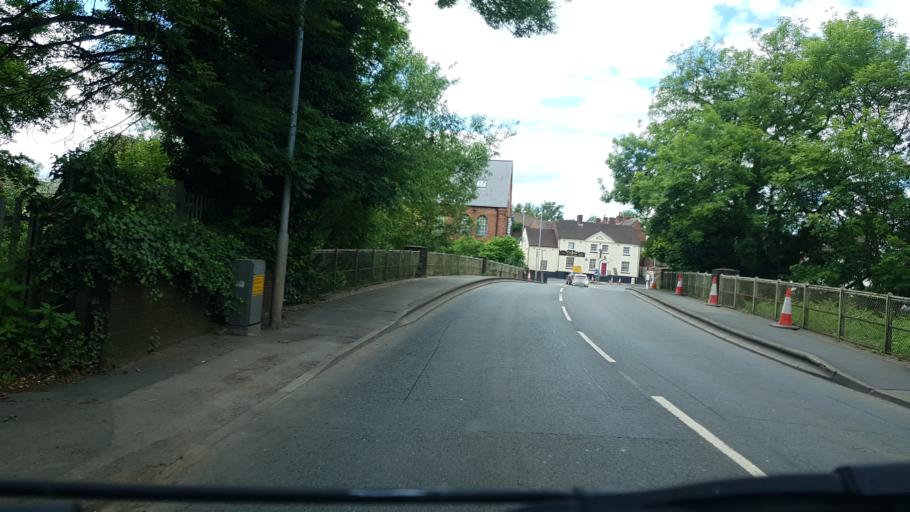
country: GB
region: England
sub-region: Worcestershire
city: Stourport-on-Severn
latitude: 52.3405
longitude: -2.2719
